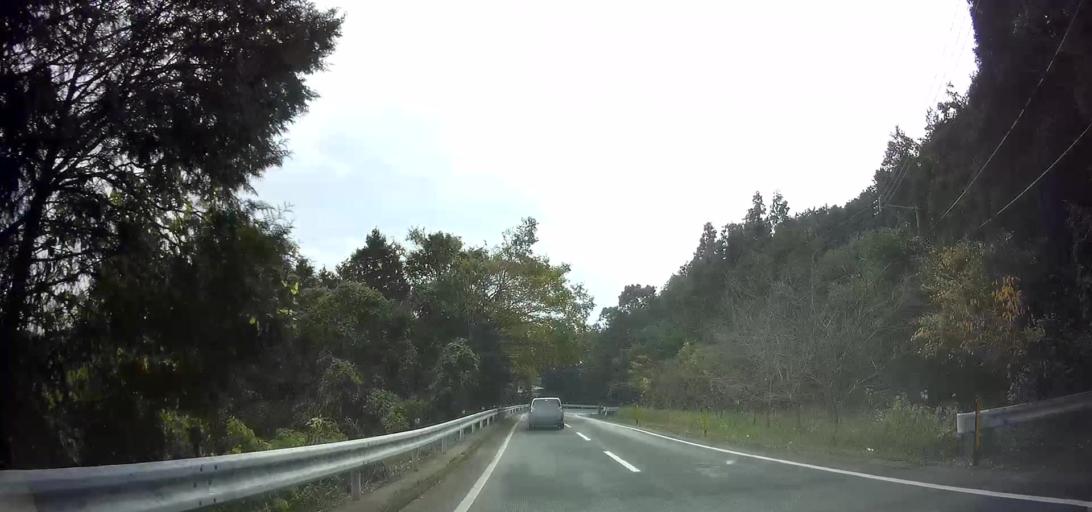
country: JP
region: Nagasaki
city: Shimabara
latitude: 32.6933
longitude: 130.2558
